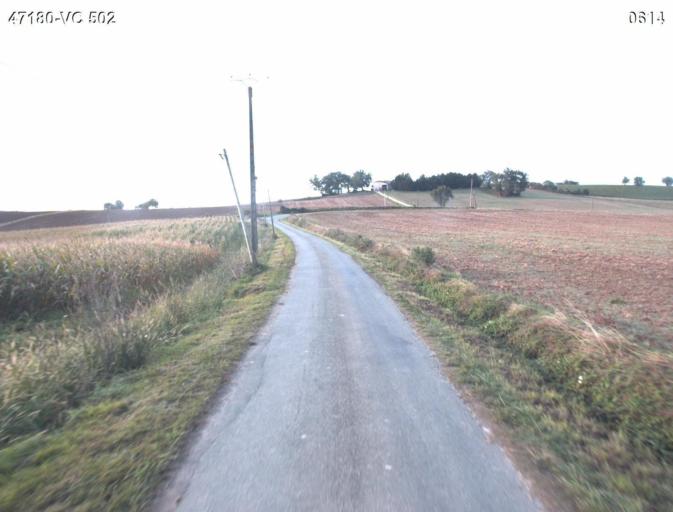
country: FR
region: Aquitaine
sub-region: Departement du Lot-et-Garonne
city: Sainte-Colombe-en-Bruilhois
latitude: 44.1636
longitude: 0.4806
